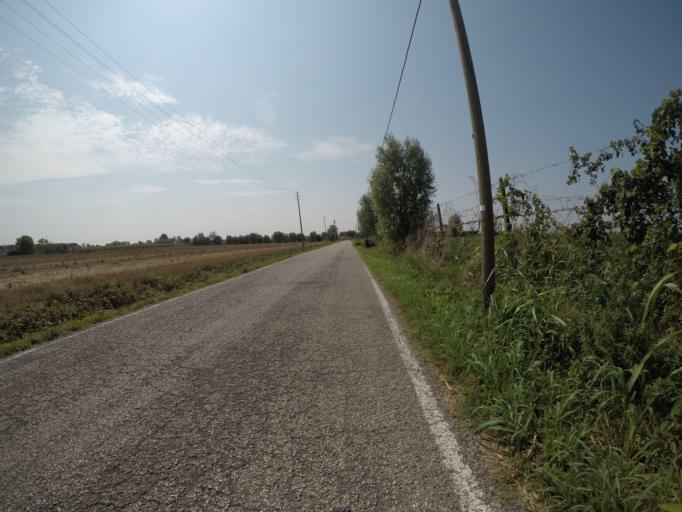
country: IT
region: Veneto
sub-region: Provincia di Rovigo
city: Lendinara
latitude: 45.1101
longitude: 11.5971
